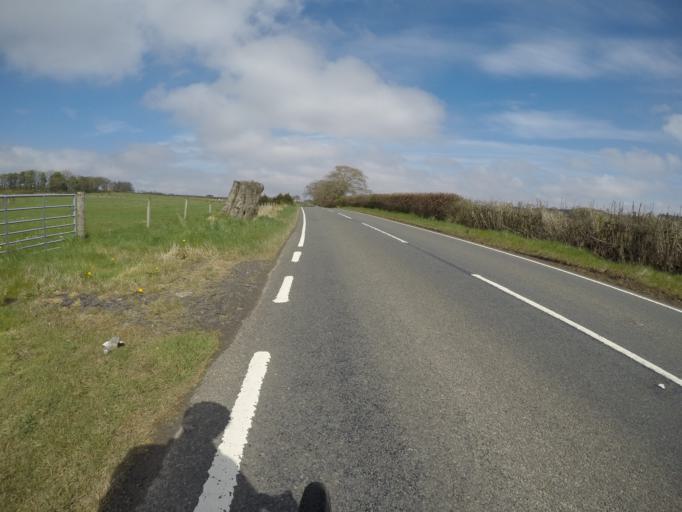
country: GB
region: Scotland
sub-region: East Ayrshire
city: Stewarton
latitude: 55.7086
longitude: -4.4588
